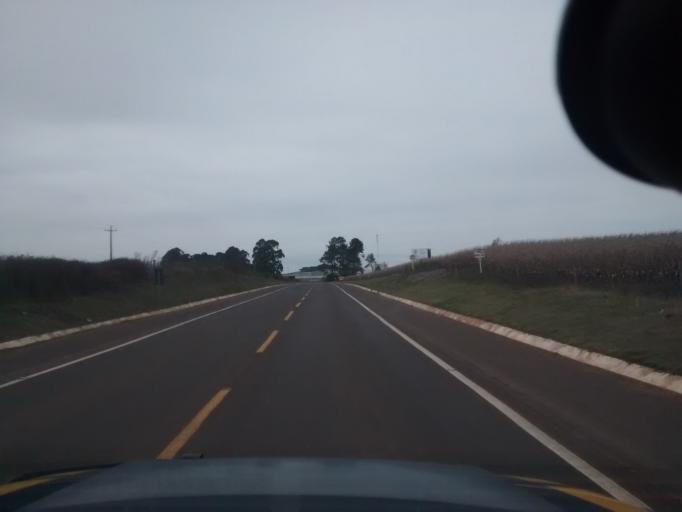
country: BR
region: Rio Grande do Sul
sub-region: Vacaria
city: Vacaria
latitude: -28.4620
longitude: -50.9787
